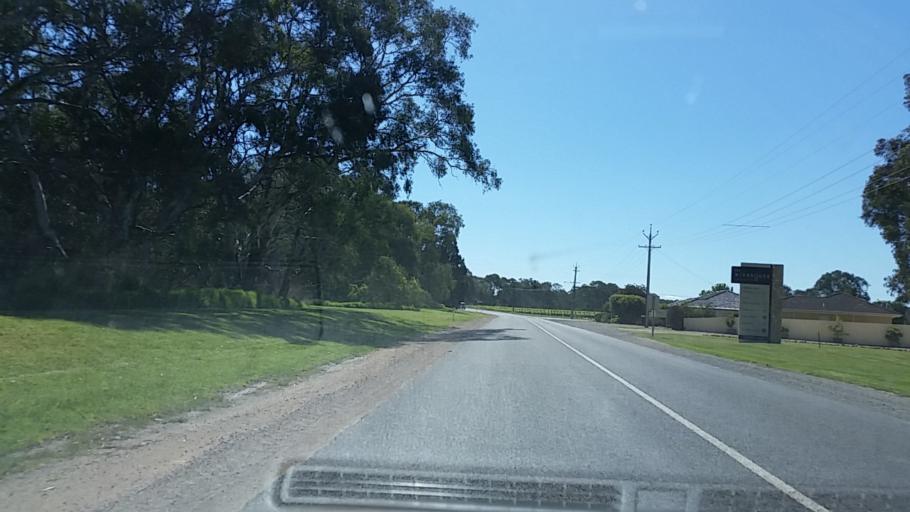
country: AU
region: South Australia
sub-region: Alexandrina
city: Langhorne Creek
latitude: -35.2971
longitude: 139.0420
